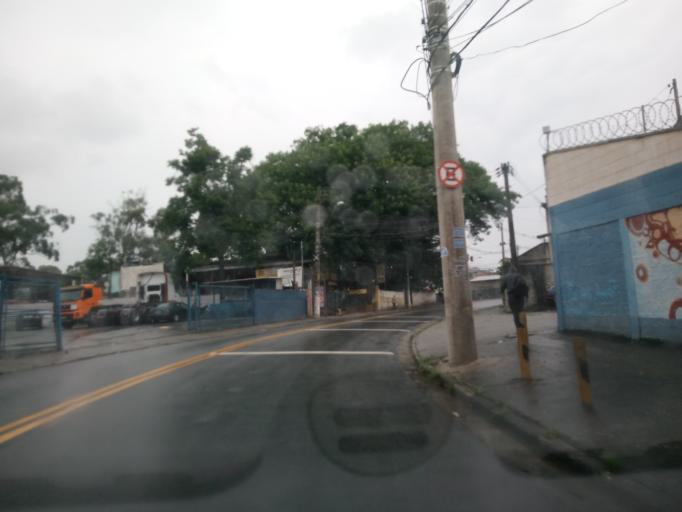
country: BR
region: Sao Paulo
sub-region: Sao Bernardo Do Campo
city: Sao Bernardo do Campo
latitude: -23.7448
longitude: -46.5547
